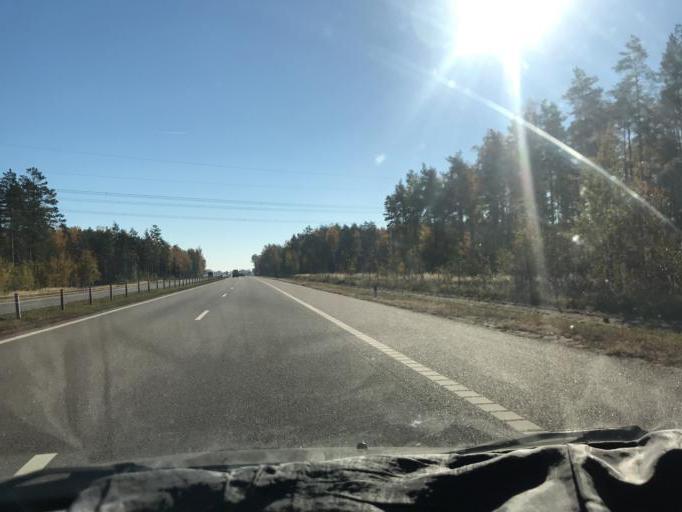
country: BY
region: Mogilev
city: Yalizava
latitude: 53.2595
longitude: 28.9008
